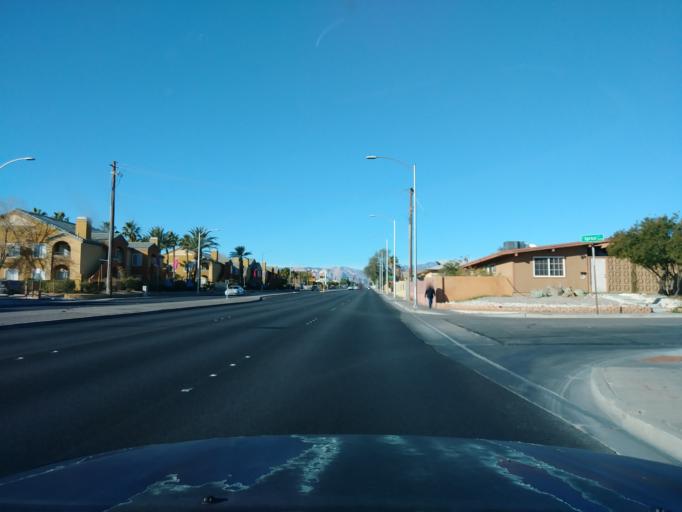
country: US
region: Nevada
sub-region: Clark County
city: Spring Valley
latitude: 36.1592
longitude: -115.2472
